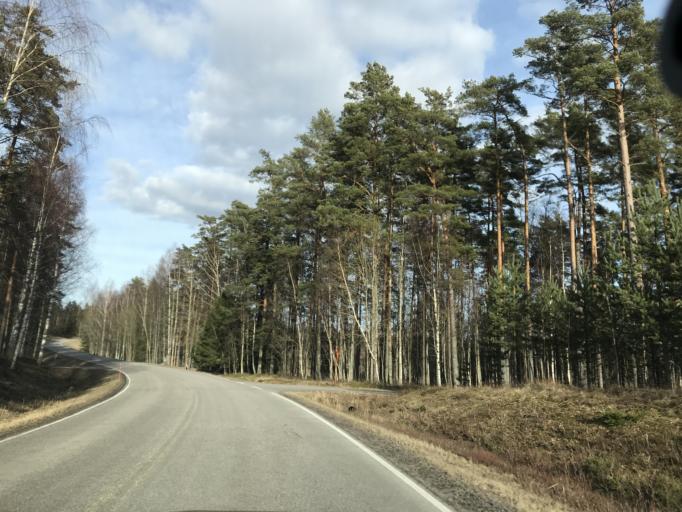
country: FI
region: Uusimaa
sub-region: Raaseporin
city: Ekenaes
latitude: 60.0732
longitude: 23.2953
